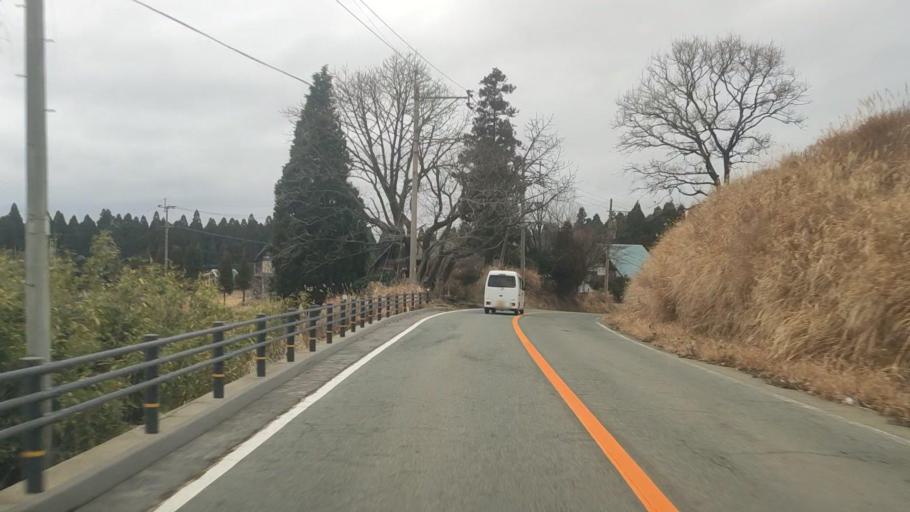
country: JP
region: Kumamoto
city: Aso
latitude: 32.9154
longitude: 131.1296
